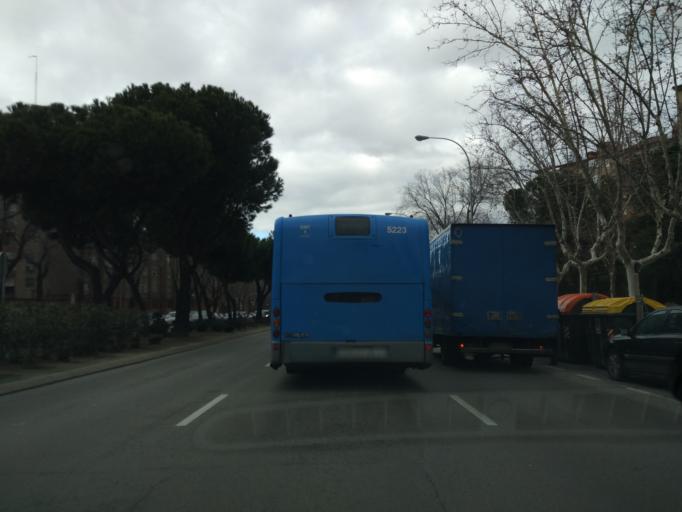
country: ES
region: Madrid
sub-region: Provincia de Madrid
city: San Blas
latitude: 40.4269
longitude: -3.6299
